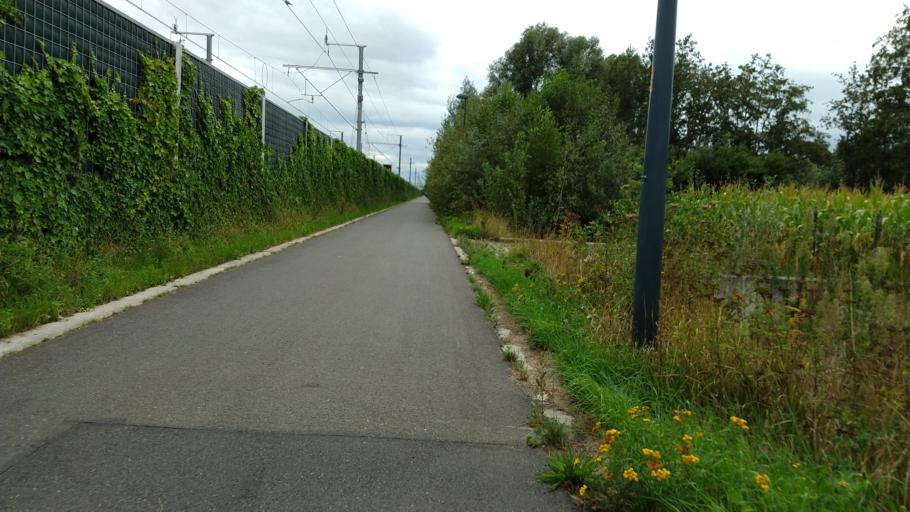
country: BE
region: Flanders
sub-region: Provincie Oost-Vlaanderen
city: Sint-Martens-Latem
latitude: 51.0497
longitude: 3.6443
